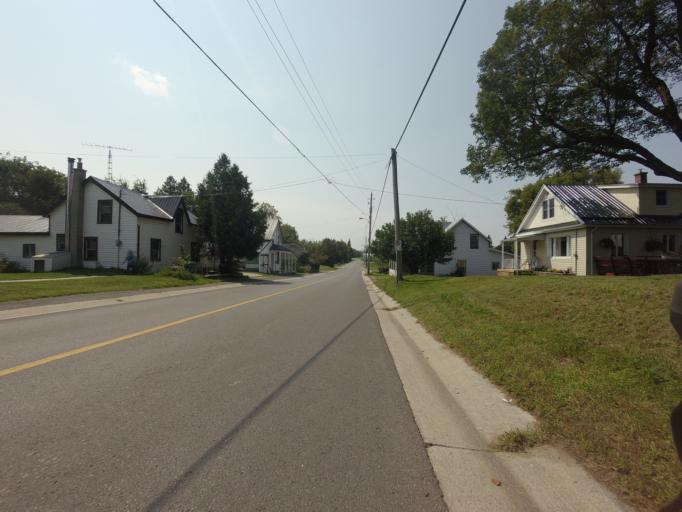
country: CA
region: Ontario
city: Skatepark
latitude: 44.6558
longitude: -76.7196
